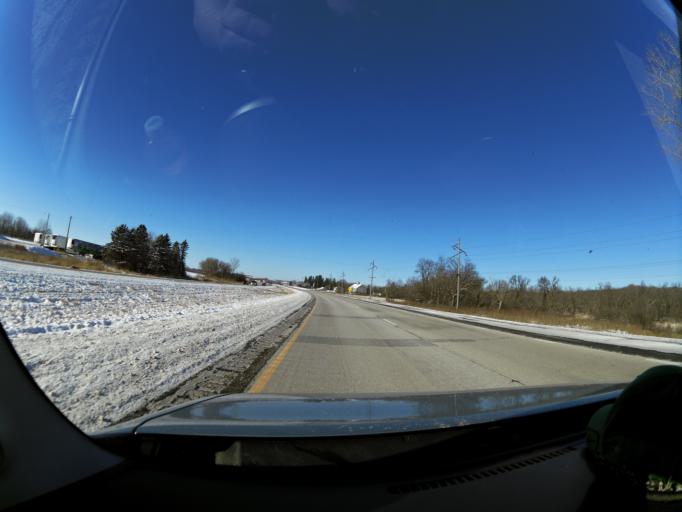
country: US
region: Minnesota
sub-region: Goodhue County
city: Zumbrota
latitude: 44.3073
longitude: -92.6907
